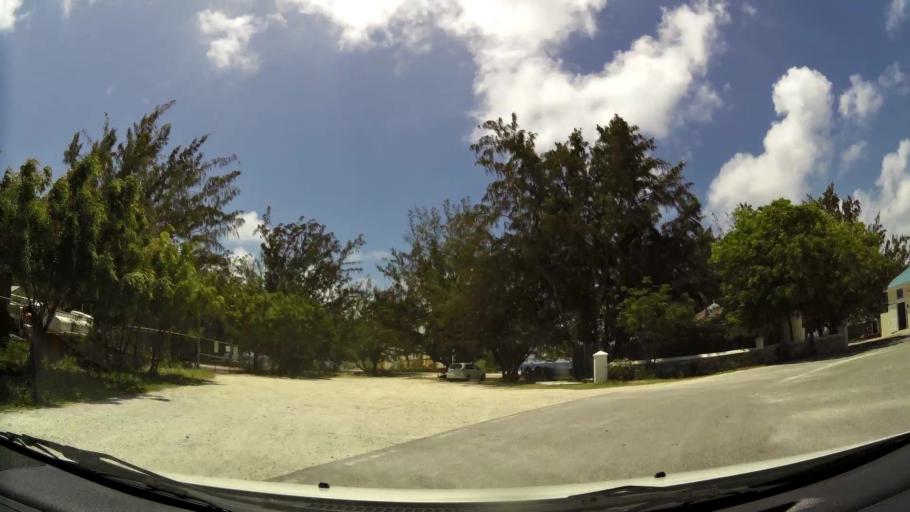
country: TC
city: Cockburn Town
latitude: 21.4365
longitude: -71.1490
